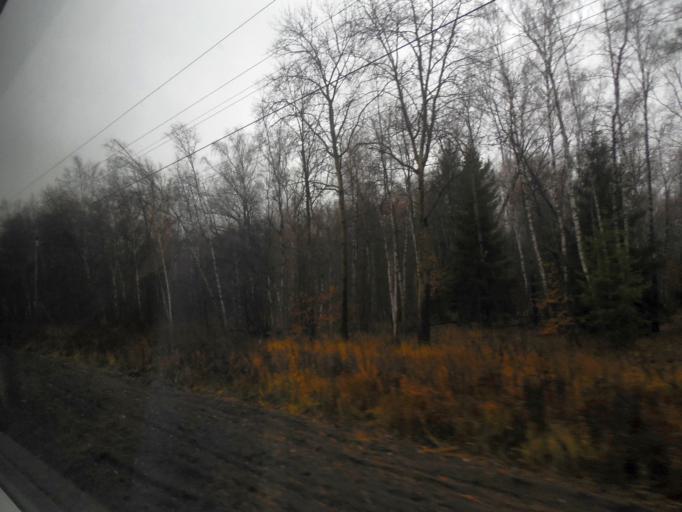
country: RU
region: Moskovskaya
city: Belyye Stolby
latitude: 55.3570
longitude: 37.8330
